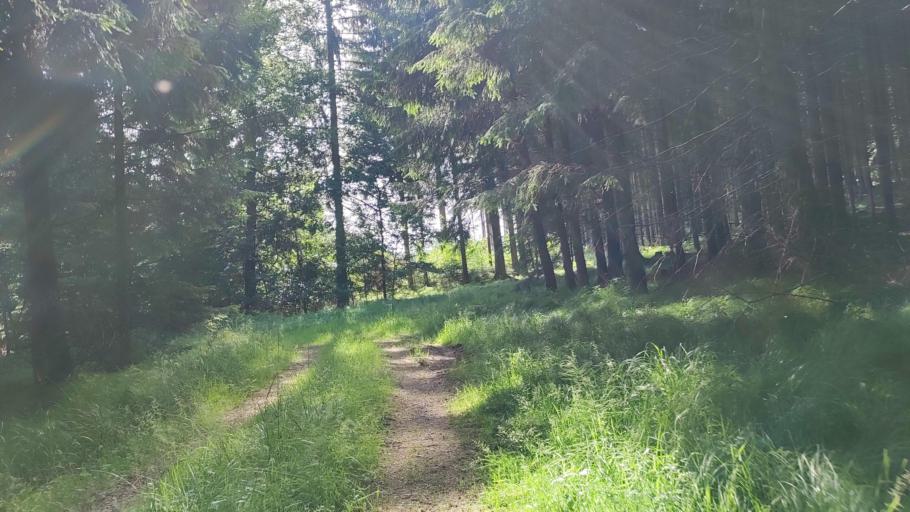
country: DE
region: Bavaria
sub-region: Swabia
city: Landensberg
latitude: 48.4106
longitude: 10.5481
